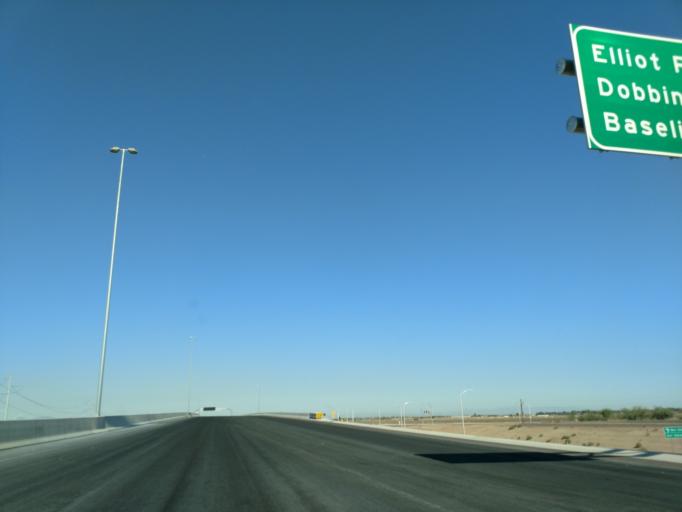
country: US
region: Arizona
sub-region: Maricopa County
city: Laveen
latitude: 33.3317
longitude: -112.1740
